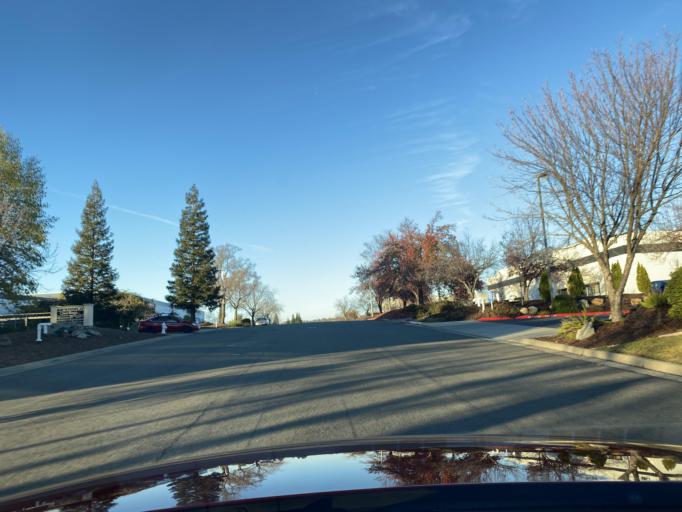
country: US
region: California
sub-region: El Dorado County
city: El Dorado Hills
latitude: 38.6377
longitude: -121.0711
